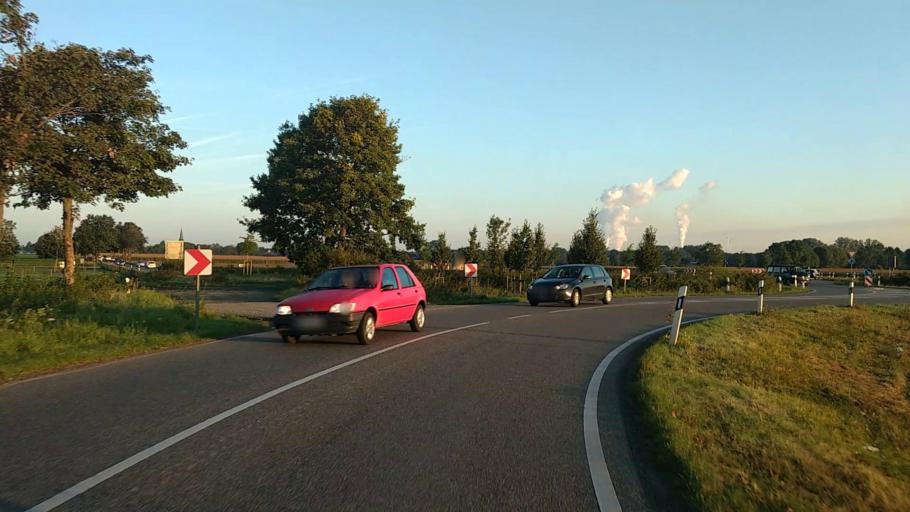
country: DE
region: North Rhine-Westphalia
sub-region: Regierungsbezirk Koln
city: Bergheim
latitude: 50.9311
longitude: 6.6418
